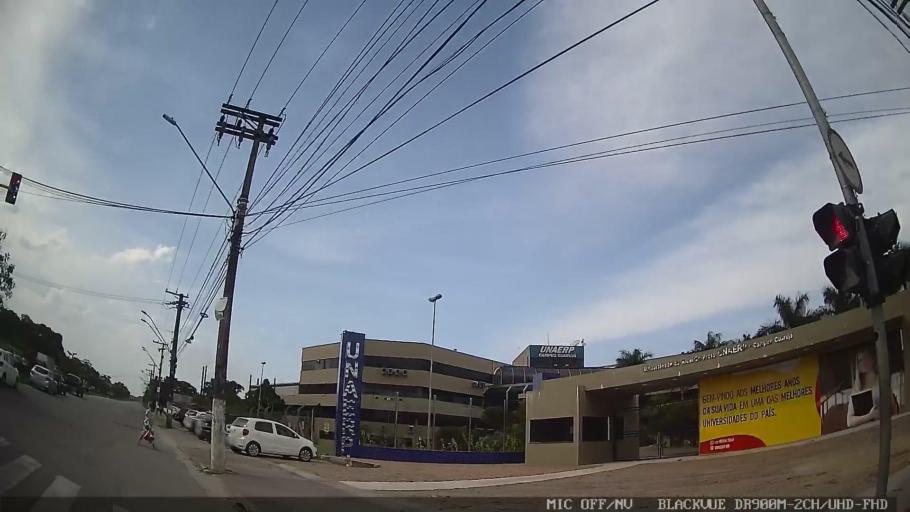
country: BR
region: Sao Paulo
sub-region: Guaruja
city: Guaruja
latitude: -23.9769
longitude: -46.2226
